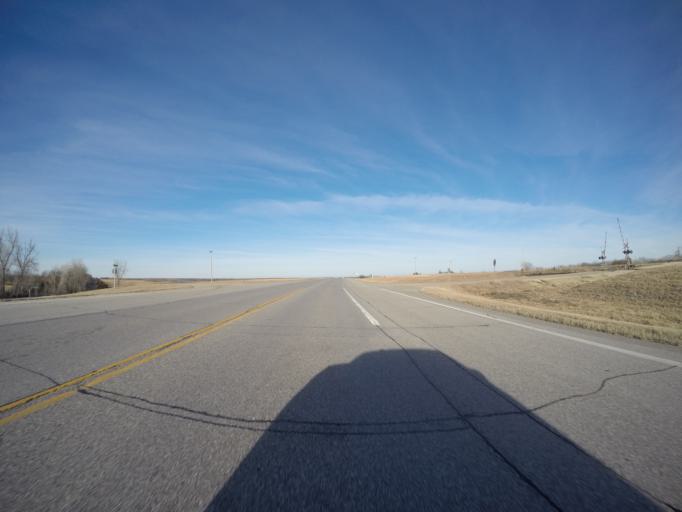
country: US
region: Kansas
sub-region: Marion County
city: Peabody
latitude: 38.1448
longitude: -97.2274
